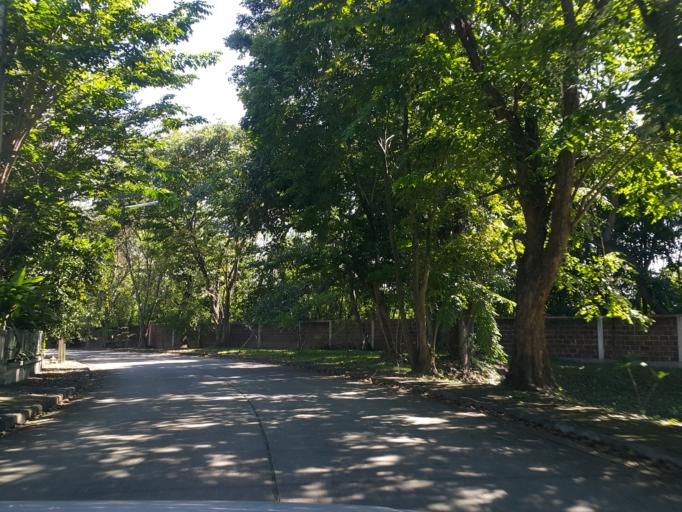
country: TH
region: Chiang Mai
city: San Sai
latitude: 18.8497
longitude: 99.0034
